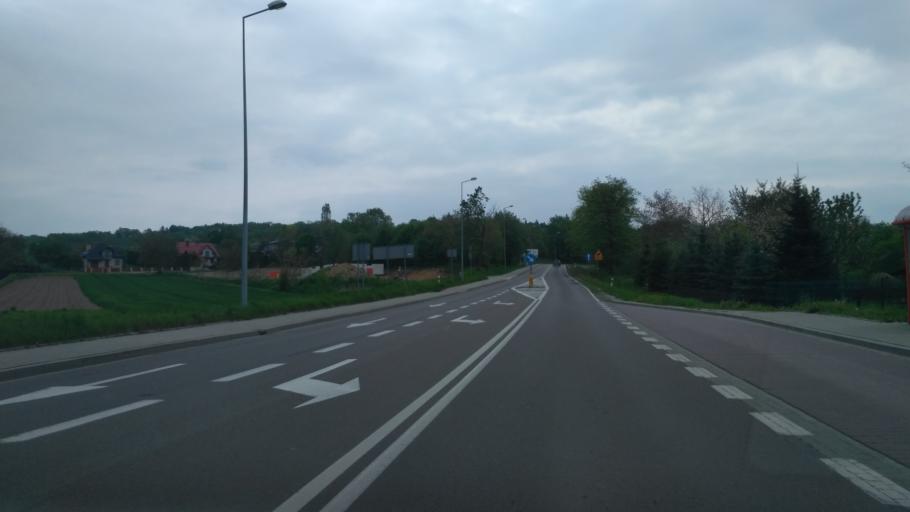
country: PL
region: Lesser Poland Voivodeship
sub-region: Powiat tarnowski
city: Tarnowiec
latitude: 49.9711
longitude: 20.9921
